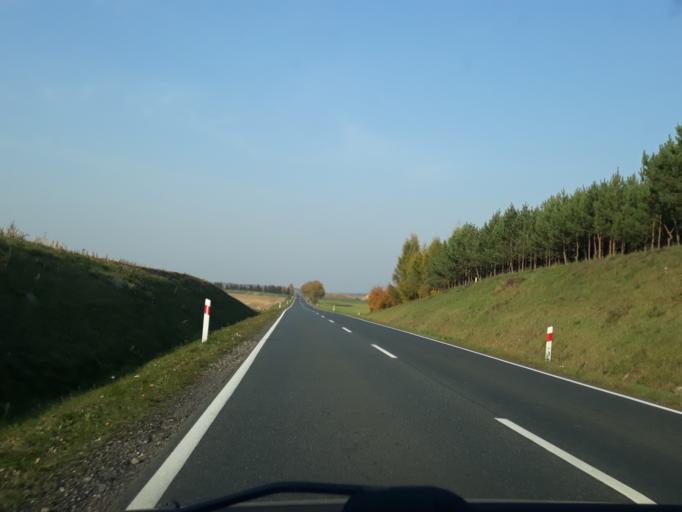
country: PL
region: Kujawsko-Pomorskie
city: Kamien Krajenski
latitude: 53.5135
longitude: 17.5104
